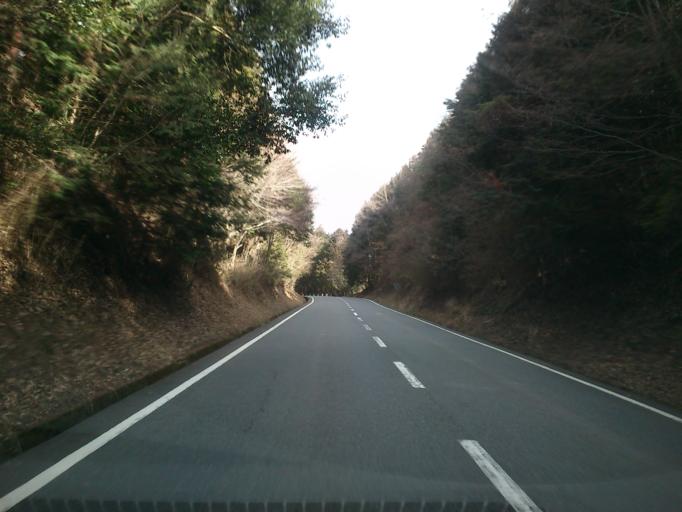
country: JP
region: Shiga Prefecture
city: Otsu-shi
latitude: 35.0416
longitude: 135.8385
